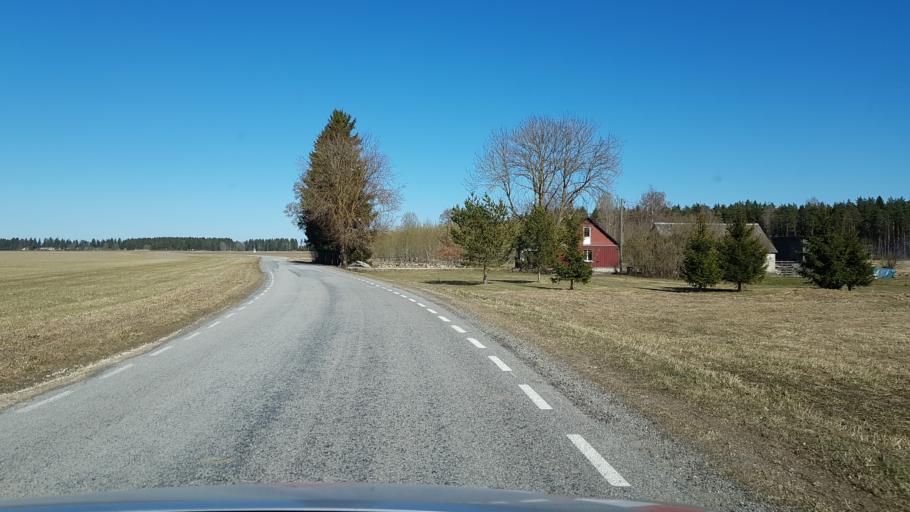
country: EE
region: Laeaene-Virumaa
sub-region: Someru vald
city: Someru
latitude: 59.3983
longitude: 26.5083
